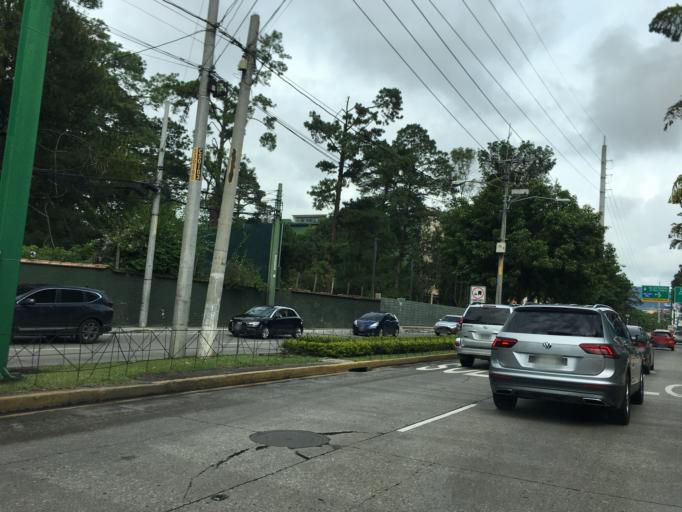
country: GT
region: Guatemala
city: Santa Catarina Pinula
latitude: 14.5998
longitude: -90.5088
